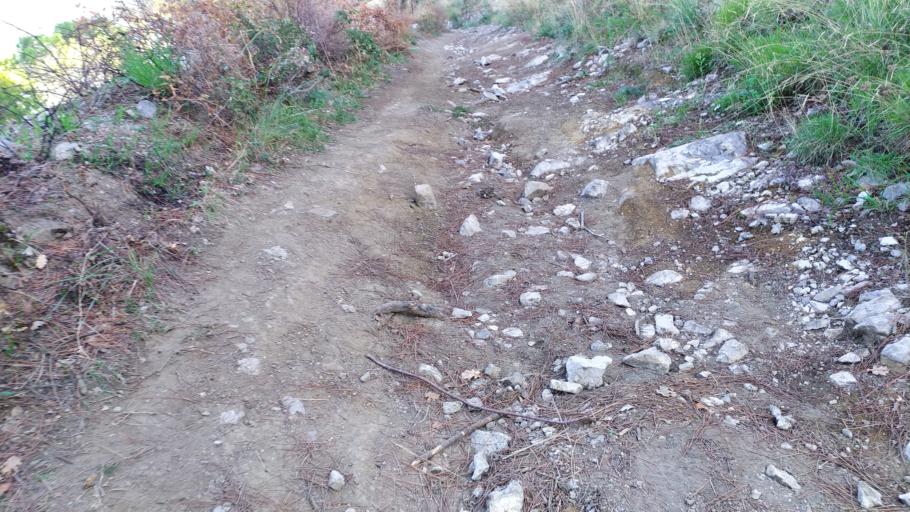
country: IT
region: Campania
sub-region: Provincia di Salerno
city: Lanzara
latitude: 40.7892
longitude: 14.6589
